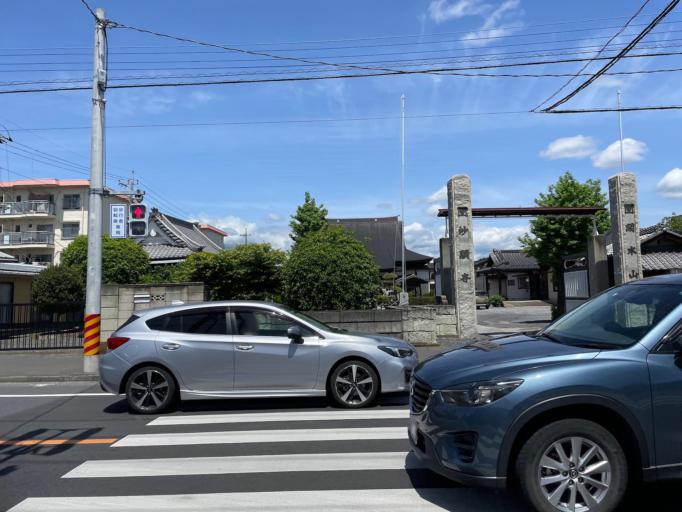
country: JP
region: Tochigi
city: Sano
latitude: 36.3222
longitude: 139.5846
